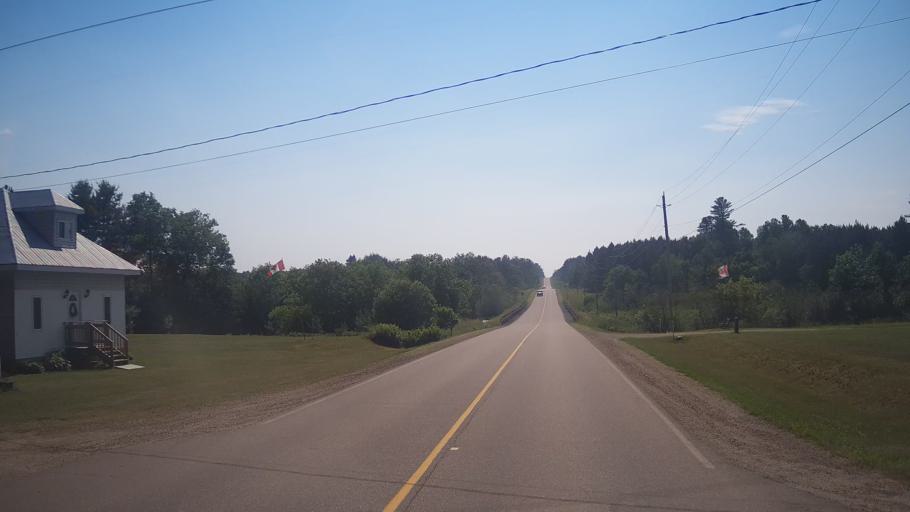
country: CA
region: Ontario
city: Pembroke
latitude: 45.6230
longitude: -77.1543
